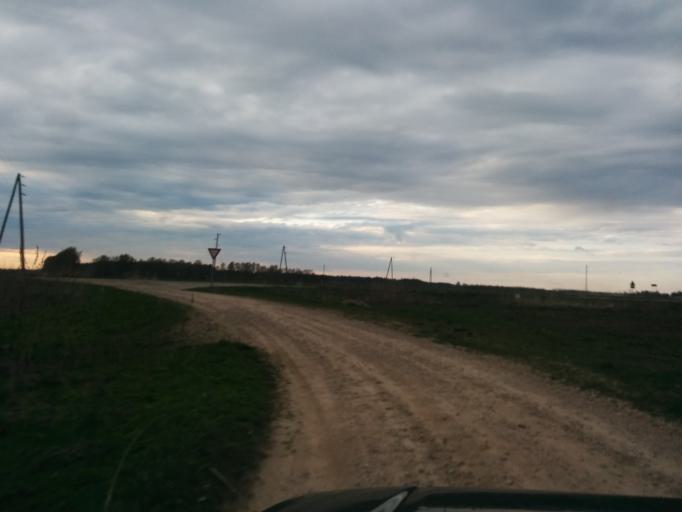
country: LV
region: Lecava
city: Iecava
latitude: 56.5952
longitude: 24.1062
